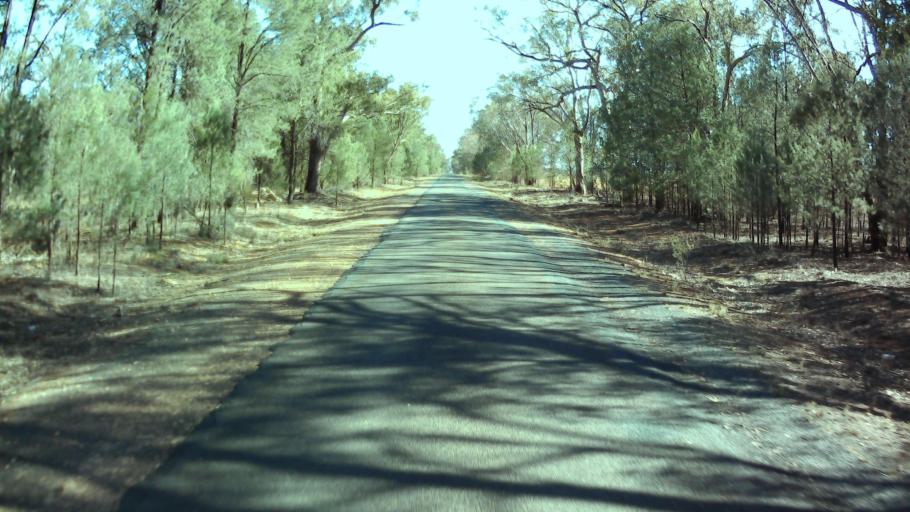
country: AU
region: New South Wales
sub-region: Weddin
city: Grenfell
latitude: -33.8104
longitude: 147.9541
